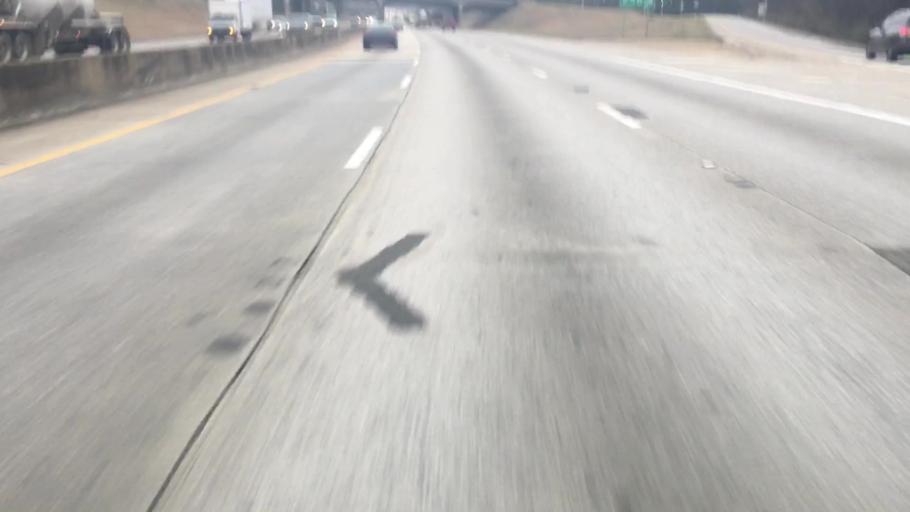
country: US
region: Alabama
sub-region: Jefferson County
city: Homewood
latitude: 33.4857
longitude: -86.8259
